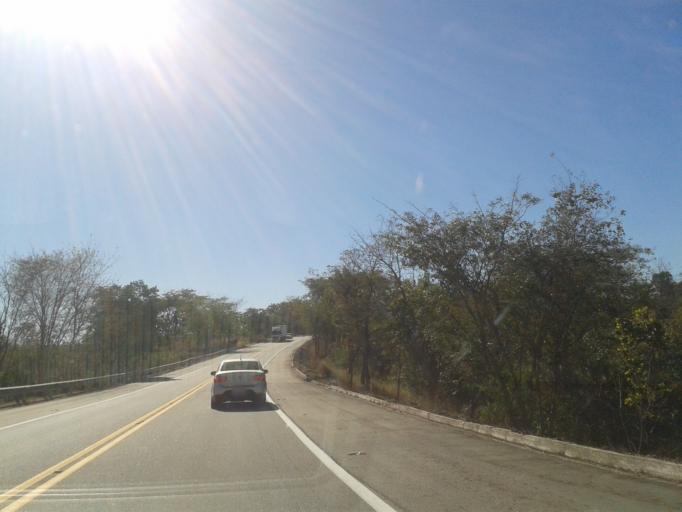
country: BR
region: Goias
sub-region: Itapuranga
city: Itapuranga
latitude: -15.6561
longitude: -50.2218
